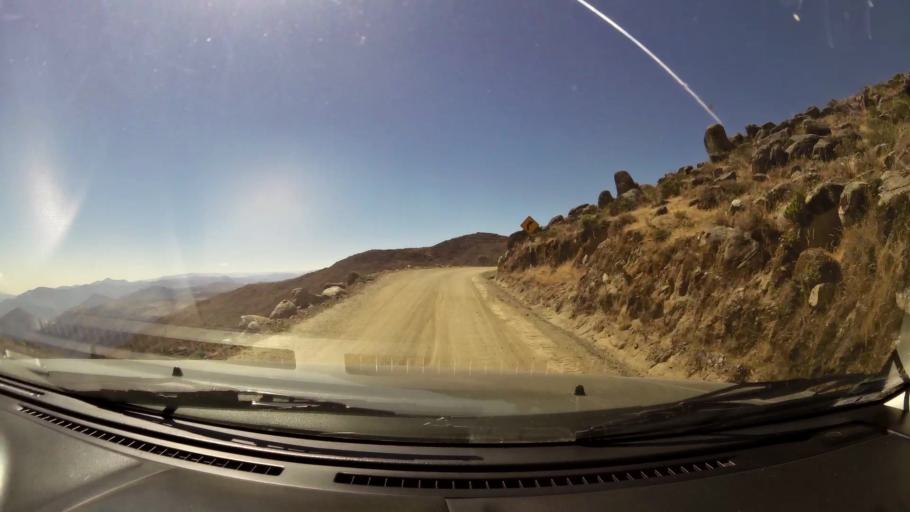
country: PE
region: Huancavelica
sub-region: Huaytara
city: Quito-Arma
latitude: -13.6347
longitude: -75.3638
